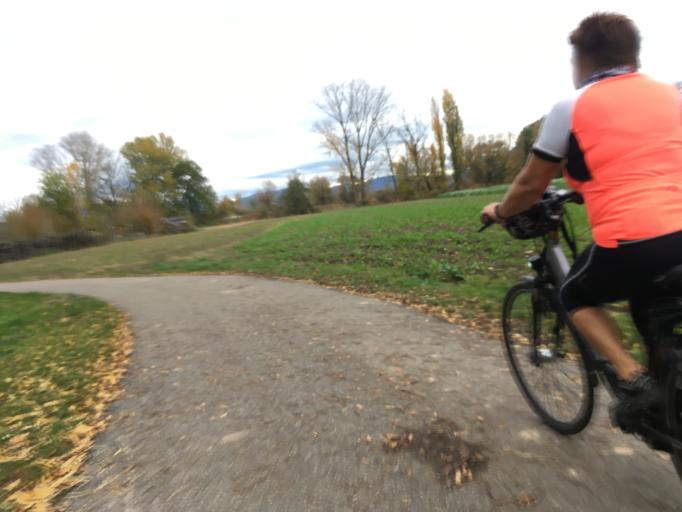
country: DE
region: Baden-Wuerttemberg
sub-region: Freiburg Region
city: Botzingen
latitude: 48.0788
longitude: 7.7341
